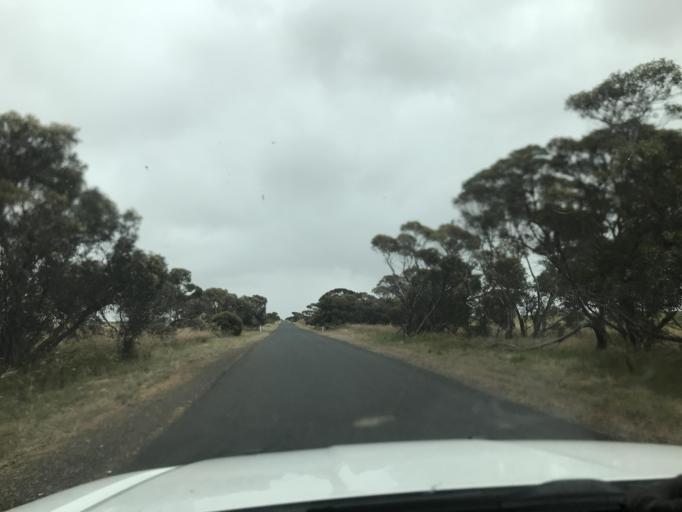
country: AU
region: South Australia
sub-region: Tatiara
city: Bordertown
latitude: -36.1181
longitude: 141.0447
